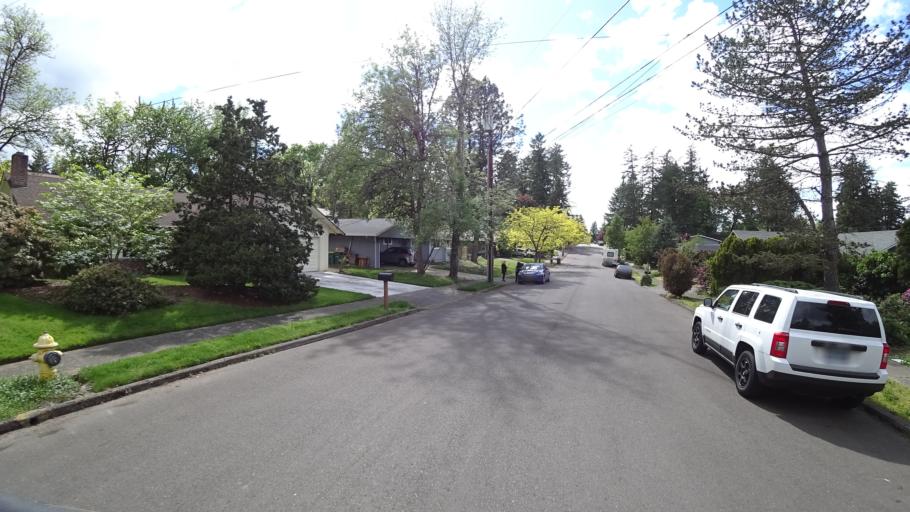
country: US
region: Oregon
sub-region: Washington County
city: Beaverton
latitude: 45.4778
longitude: -122.8201
